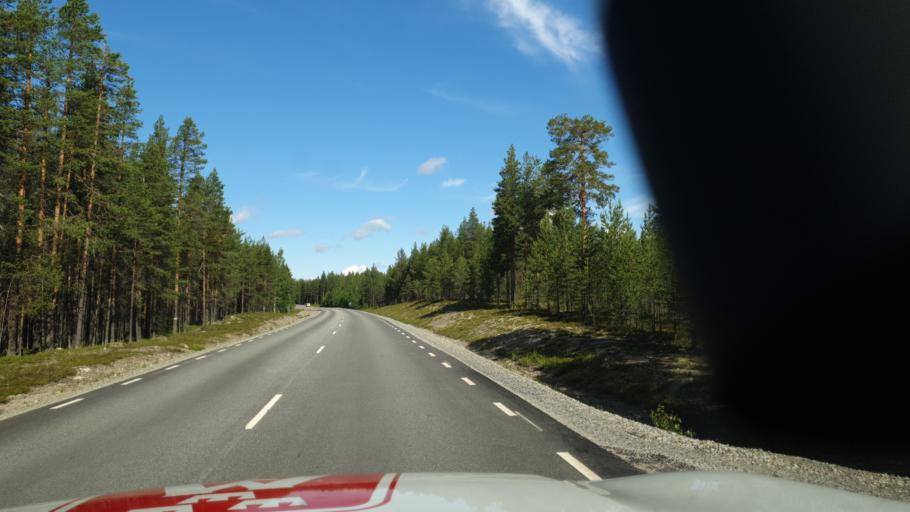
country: SE
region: Vaesterbotten
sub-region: Norsjo Kommun
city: Norsjoe
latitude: 64.6785
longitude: 19.2503
